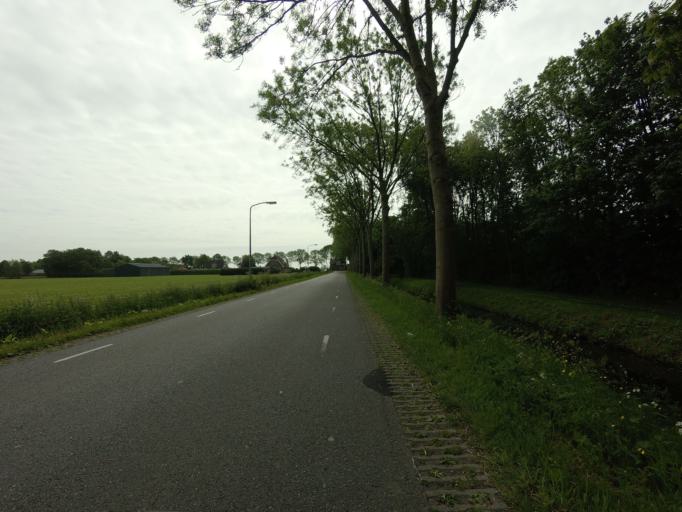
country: NL
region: North Holland
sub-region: Gemeente Hoorn
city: Hoorn
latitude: 52.6920
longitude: 5.0679
